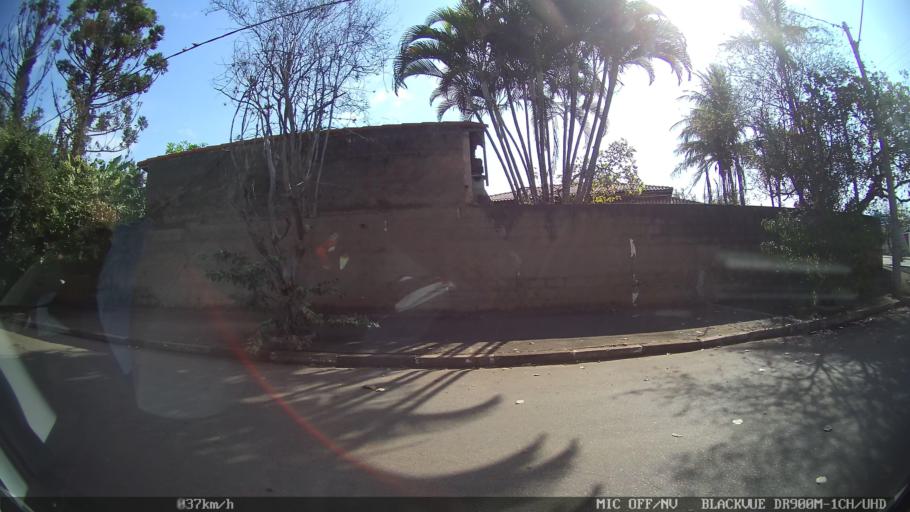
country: BR
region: Sao Paulo
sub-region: Paulinia
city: Paulinia
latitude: -22.7701
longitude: -47.1418
